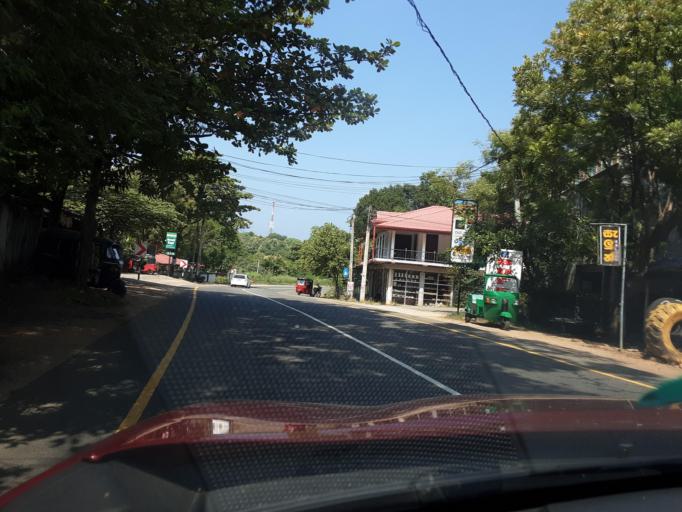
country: LK
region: Uva
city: Badulla
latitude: 7.2851
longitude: 81.0413
